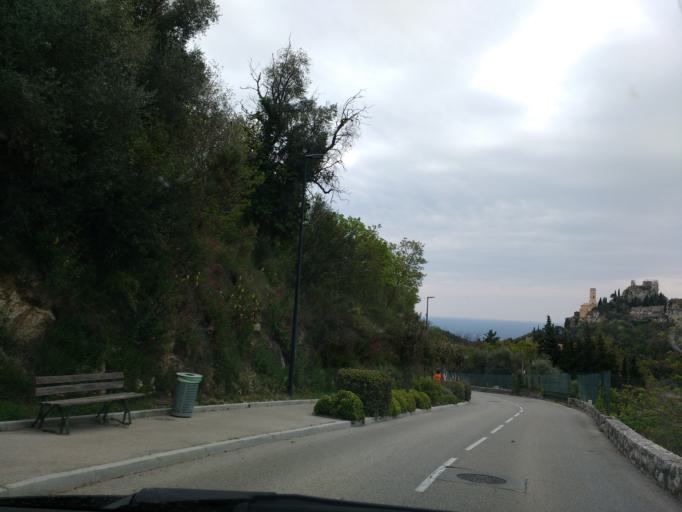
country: FR
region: Provence-Alpes-Cote d'Azur
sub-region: Departement des Alpes-Maritimes
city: Eze
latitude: 43.7330
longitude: 7.3574
